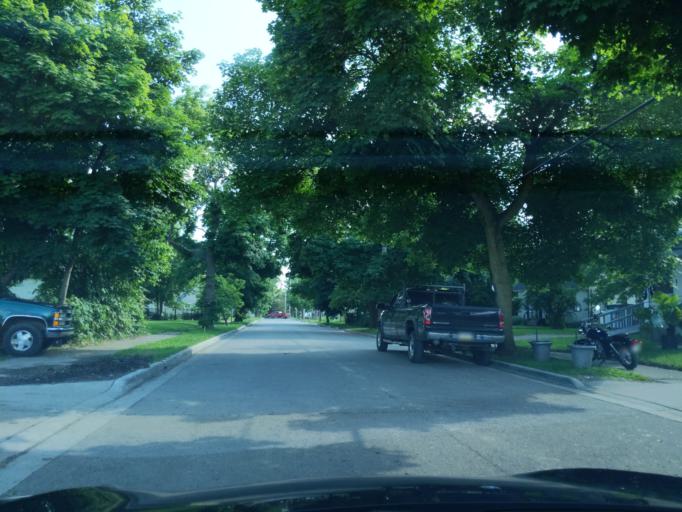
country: US
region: Michigan
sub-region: Ingham County
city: Lansing
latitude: 42.7587
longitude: -84.5362
